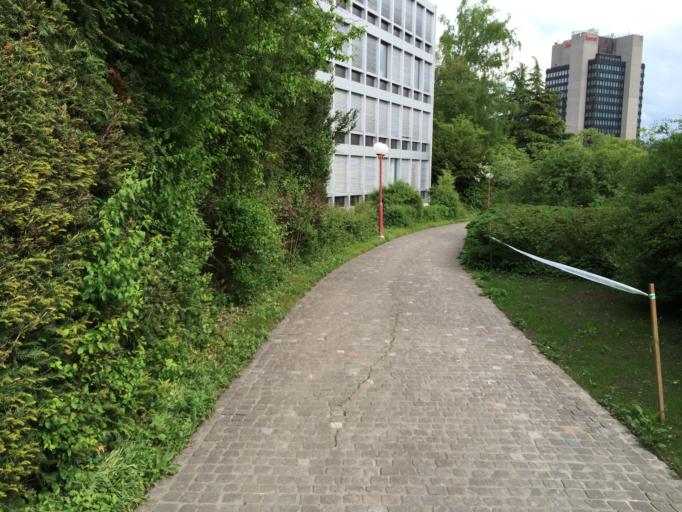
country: CH
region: Zurich
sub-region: Bezirk Zuerich
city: Zuerich (Kreis 5) / Gewerbeschule
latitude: 47.3844
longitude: 8.5385
